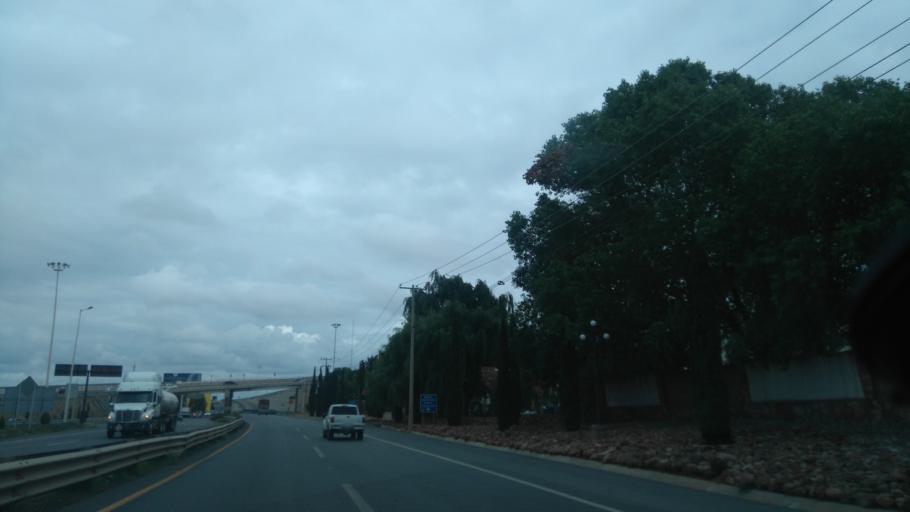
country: MX
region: Zacatecas
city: Zacatecas
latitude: 22.7736
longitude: -102.6199
